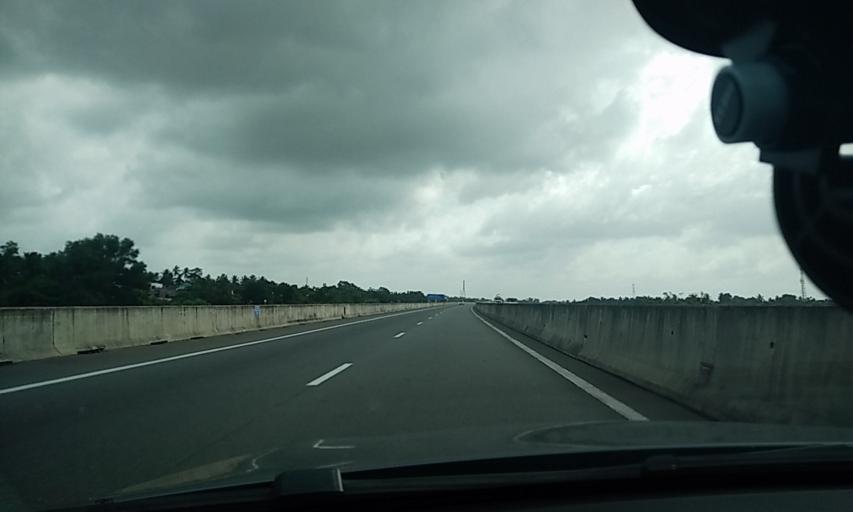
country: LK
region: Western
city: Mulleriyawa
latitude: 6.9038
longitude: 79.9798
